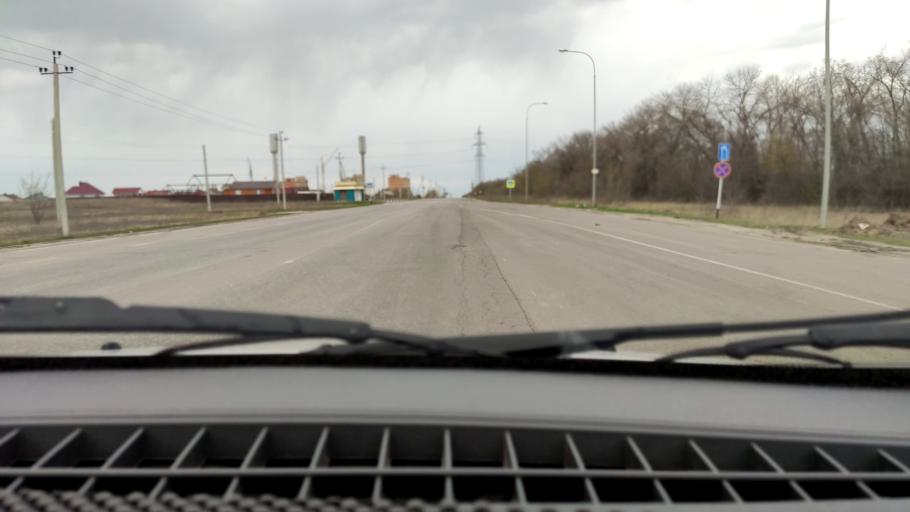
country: RU
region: Voronezj
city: Novaya Usman'
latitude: 51.6221
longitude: 39.3352
